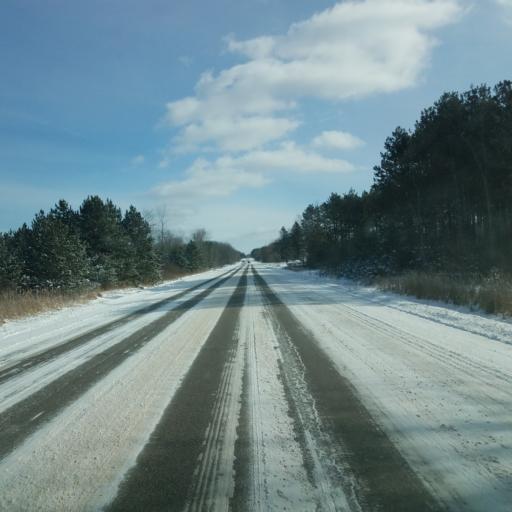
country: US
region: Michigan
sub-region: Osceola County
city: Evart
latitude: 43.9008
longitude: -85.1403
